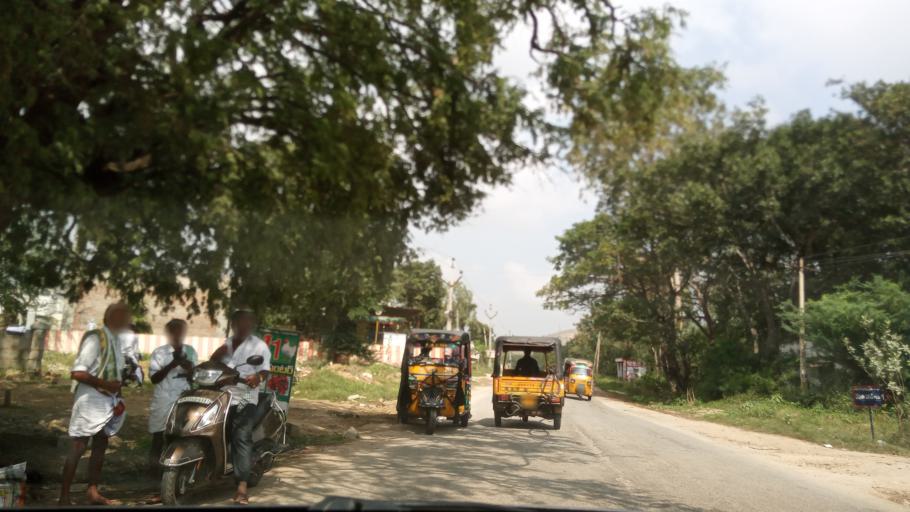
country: IN
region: Andhra Pradesh
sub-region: Chittoor
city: Madanapalle
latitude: 13.5718
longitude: 78.5166
